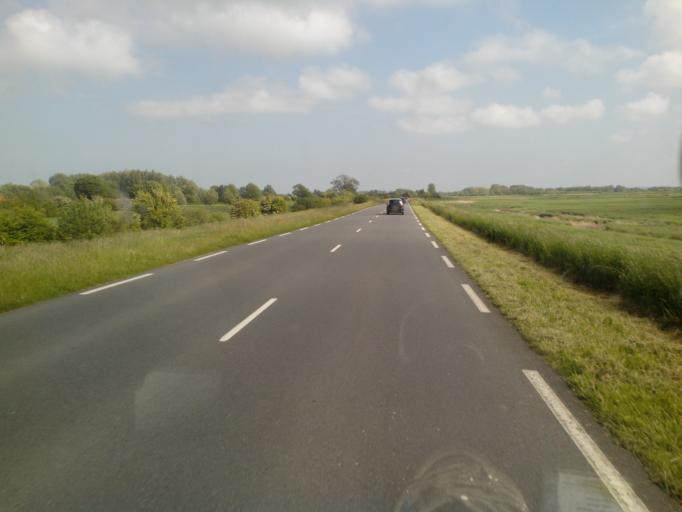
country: FR
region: Picardie
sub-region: Departement de la Somme
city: Saint-Valery-sur-Somme
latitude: 50.2078
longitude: 1.6799
